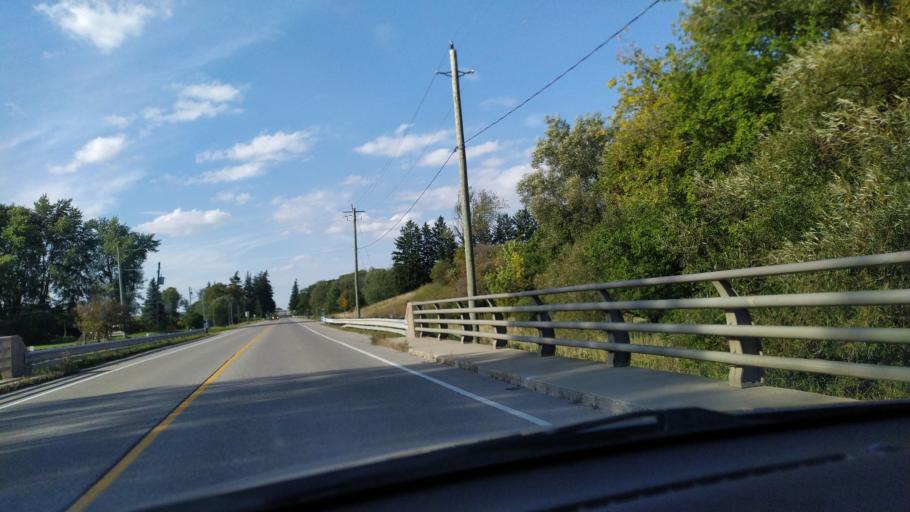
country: CA
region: Ontario
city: Ingersoll
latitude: 43.1596
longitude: -80.9030
